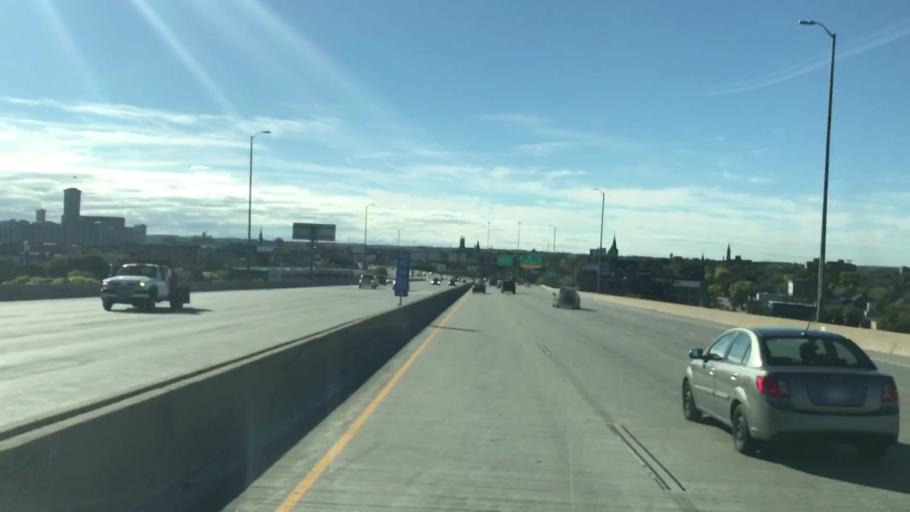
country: US
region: Wisconsin
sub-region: Milwaukee County
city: Milwaukee
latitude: 43.0270
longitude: -87.9223
